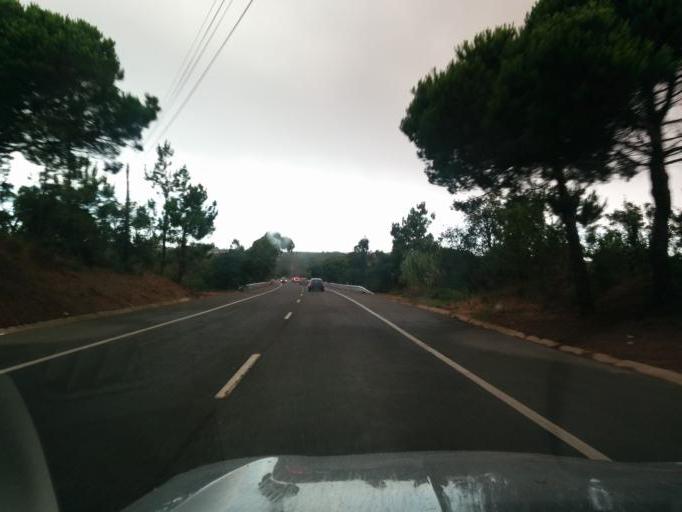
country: PT
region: Beja
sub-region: Odemira
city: Vila Nova de Milfontes
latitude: 37.7205
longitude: -8.7670
